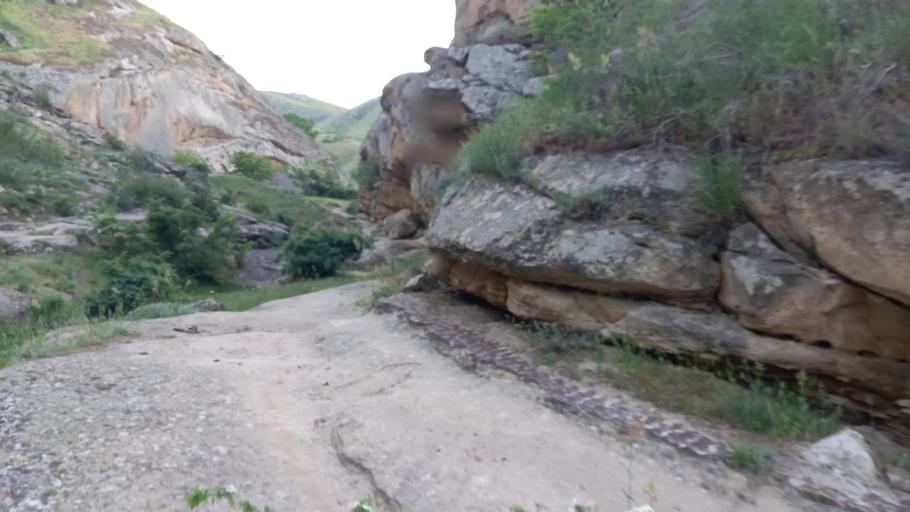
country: RU
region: Dagestan
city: Korkmaskala
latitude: 42.9788
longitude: 47.2445
